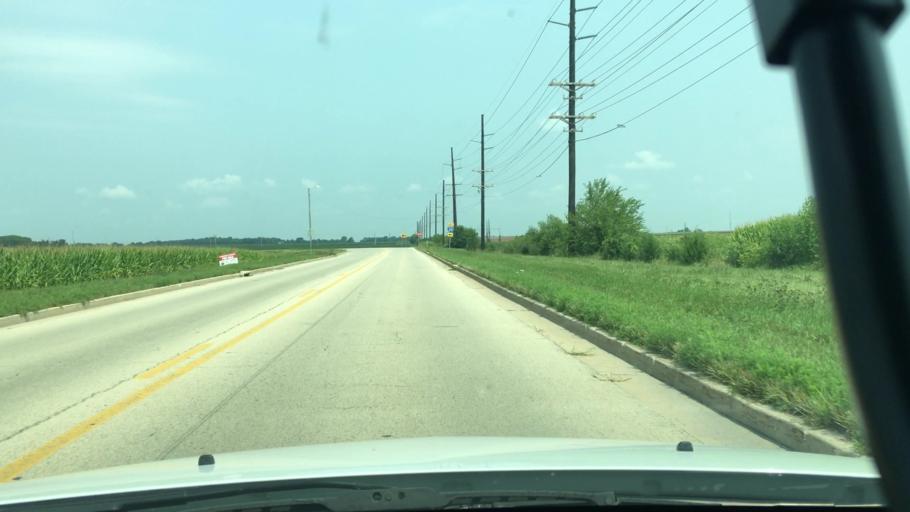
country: US
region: Illinois
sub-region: Ogle County
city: Hillcrest
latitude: 41.9399
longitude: -89.0548
